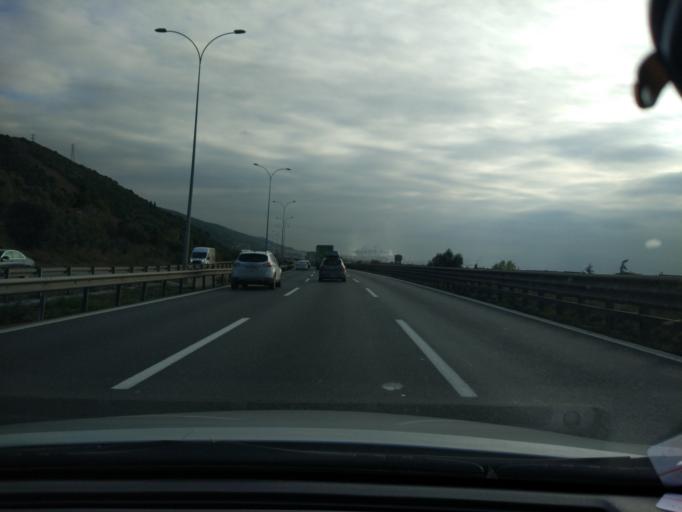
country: TR
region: Kocaeli
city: Hereke
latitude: 40.7789
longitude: 29.6757
